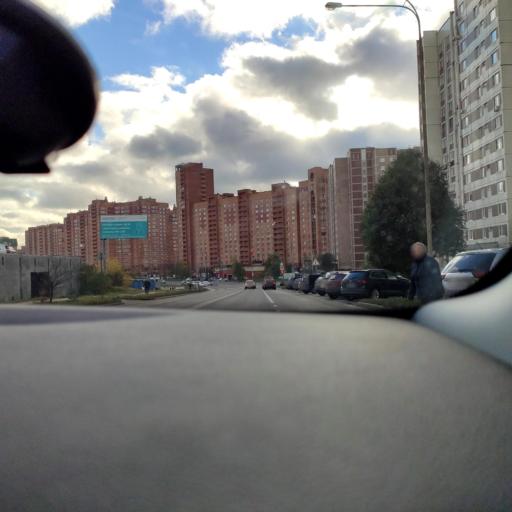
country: RU
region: Moskovskaya
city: Kotel'niki
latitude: 55.6344
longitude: 37.8514
